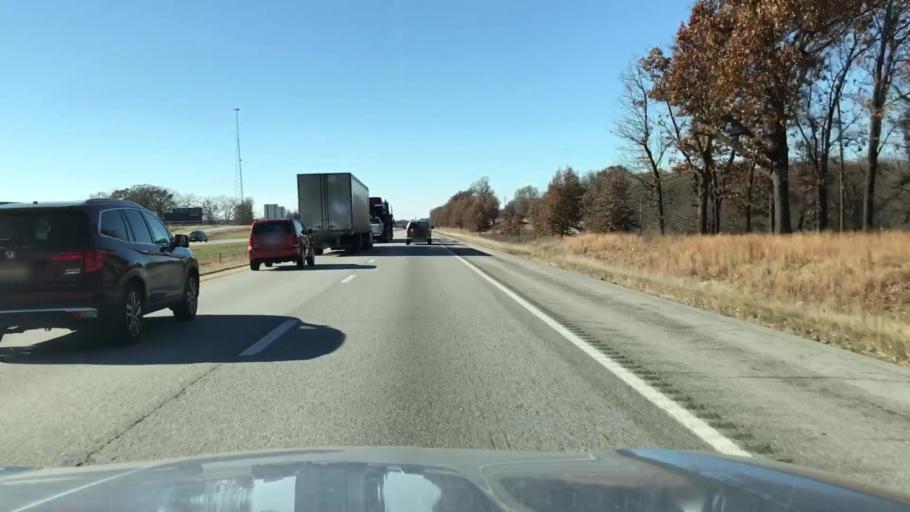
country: US
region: Missouri
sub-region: Jasper County
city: Duenweg
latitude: 37.0822
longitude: -94.3476
